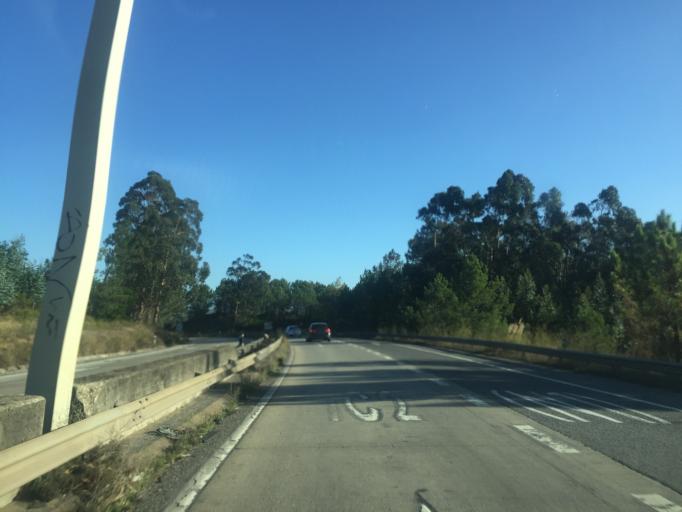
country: PT
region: Santarem
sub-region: Rio Maior
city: Rio Maior
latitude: 39.3090
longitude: -8.9377
